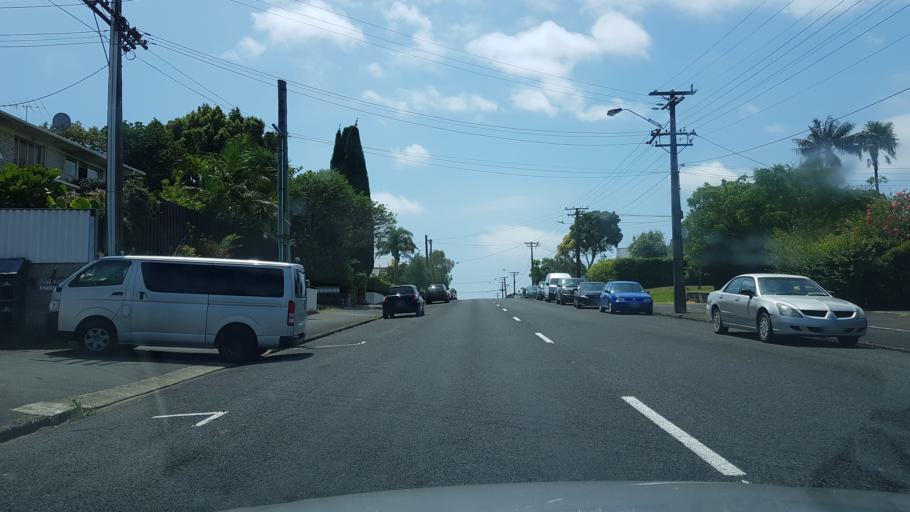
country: NZ
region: Auckland
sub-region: Auckland
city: Auckland
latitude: -36.8243
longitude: 174.8038
